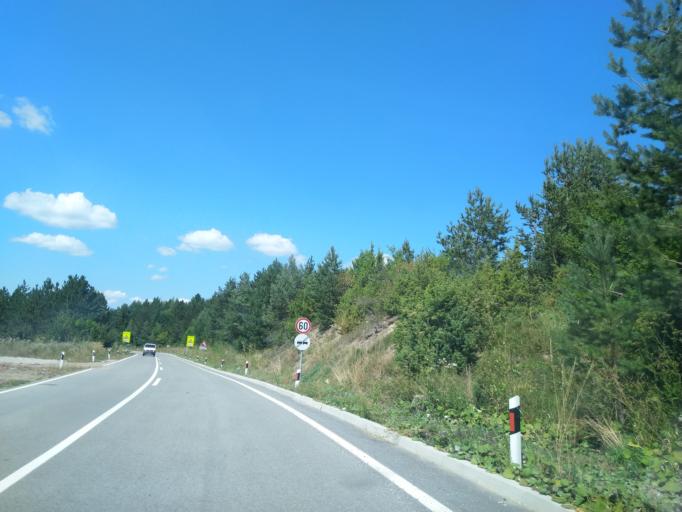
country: RS
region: Central Serbia
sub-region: Zlatiborski Okrug
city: Sjenica
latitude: 43.3112
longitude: 19.8980
